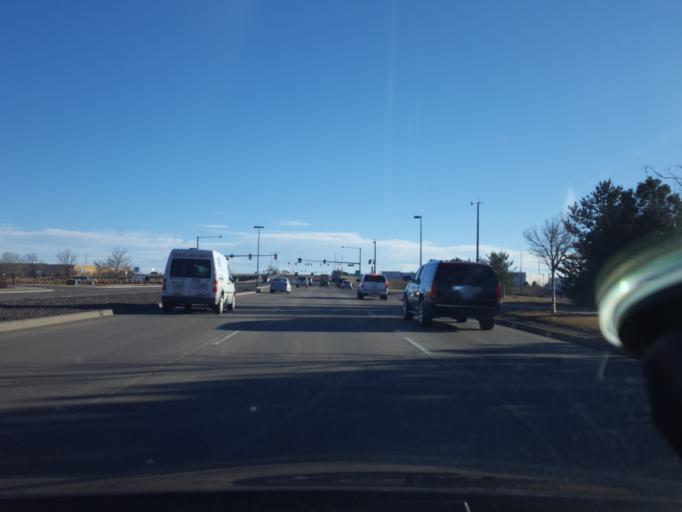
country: US
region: Colorado
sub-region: Adams County
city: Aurora
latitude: 39.7634
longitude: -104.7723
